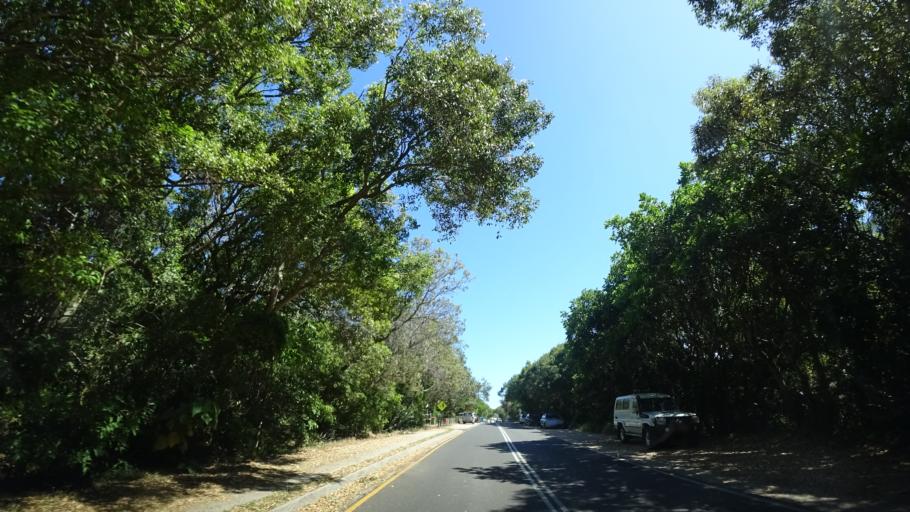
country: AU
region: Queensland
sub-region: Sunshine Coast
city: Mooloolaba
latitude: -26.6360
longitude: 153.1016
